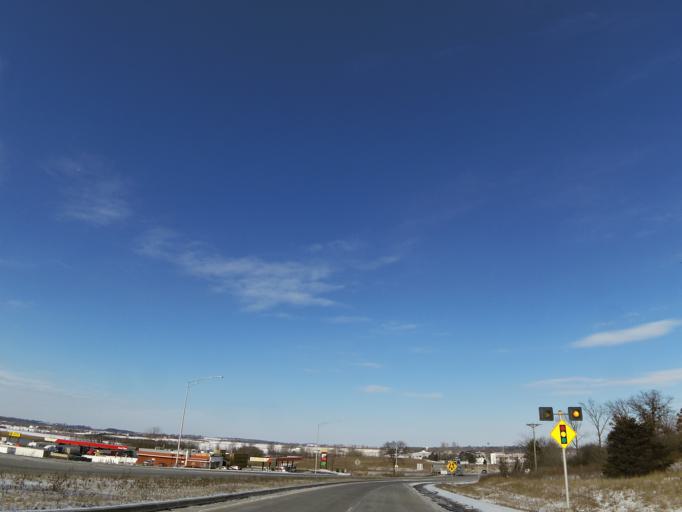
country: US
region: Wisconsin
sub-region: Saint Croix County
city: Roberts
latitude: 44.9611
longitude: -92.5593
